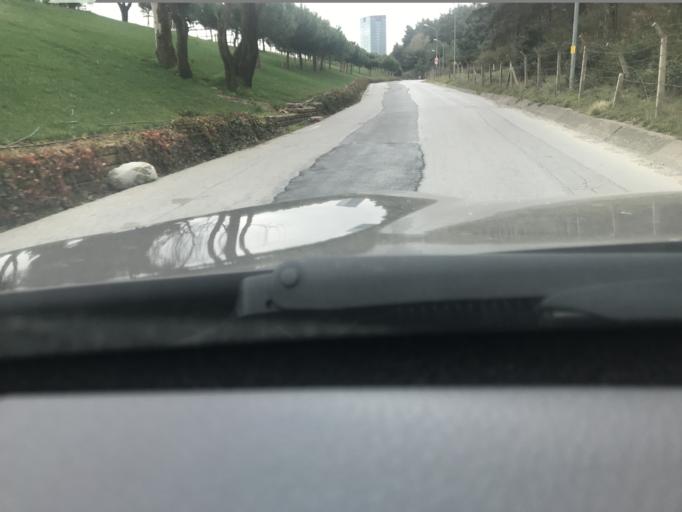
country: TR
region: Istanbul
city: Umraniye
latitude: 41.0328
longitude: 29.1367
